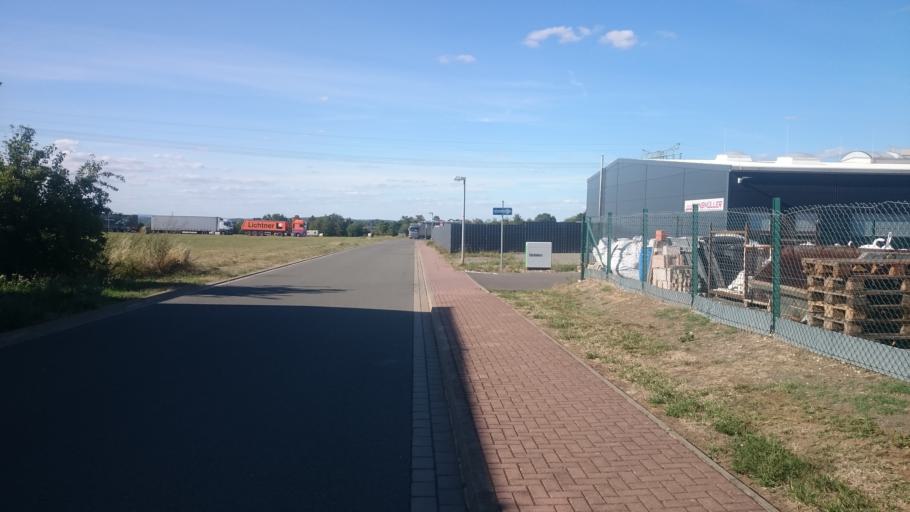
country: DE
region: Saxony-Anhalt
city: Gernrode
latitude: 51.7393
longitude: 11.1486
